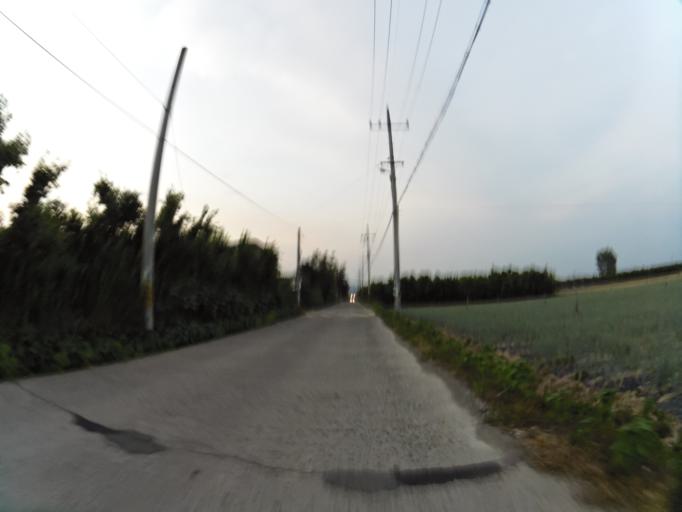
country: KR
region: Gyeongsangbuk-do
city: Gyeongsan-si
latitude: 35.8541
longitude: 128.7490
